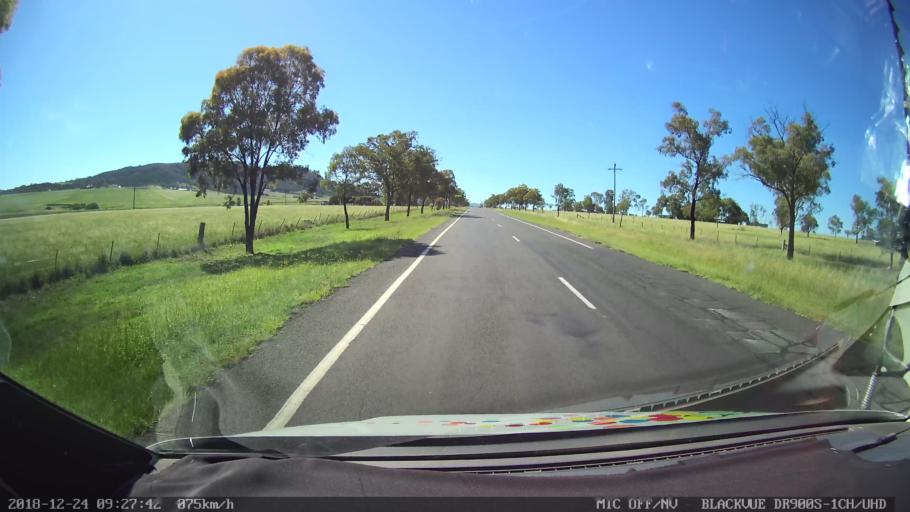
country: AU
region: New South Wales
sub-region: Liverpool Plains
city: Quirindi
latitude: -31.5306
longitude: 150.6831
